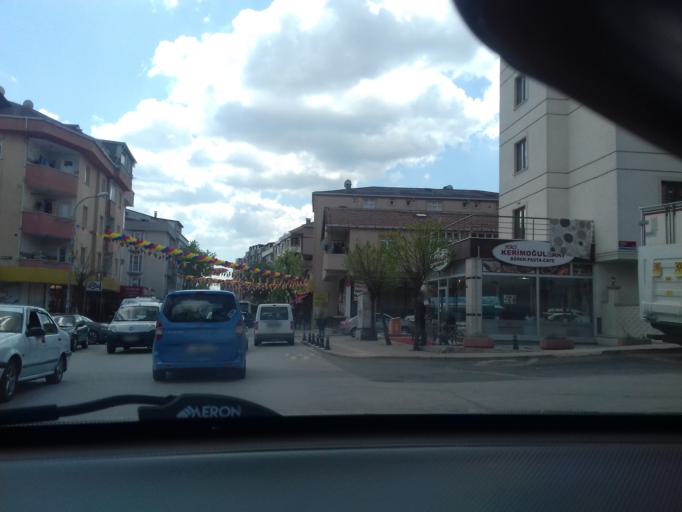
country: TR
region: Istanbul
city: Pendik
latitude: 40.8852
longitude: 29.2864
